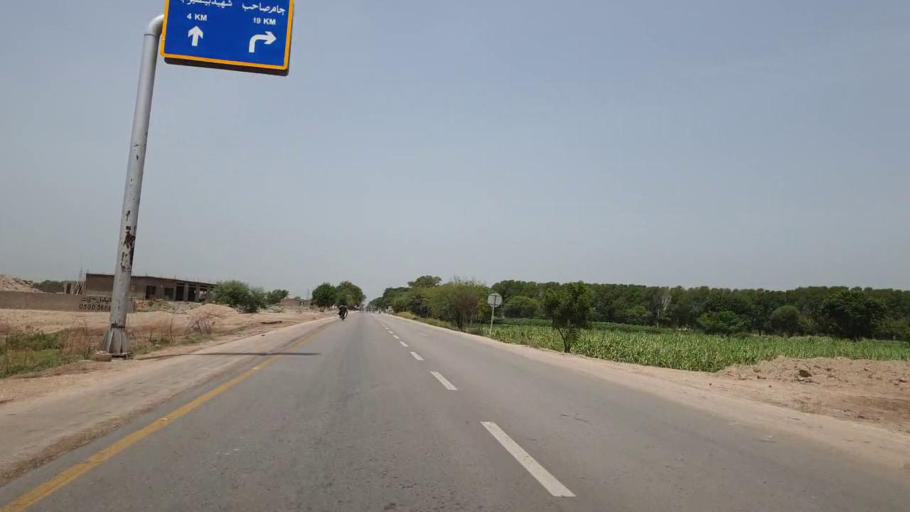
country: PK
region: Sindh
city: Nawabshah
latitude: 26.2463
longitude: 68.4599
